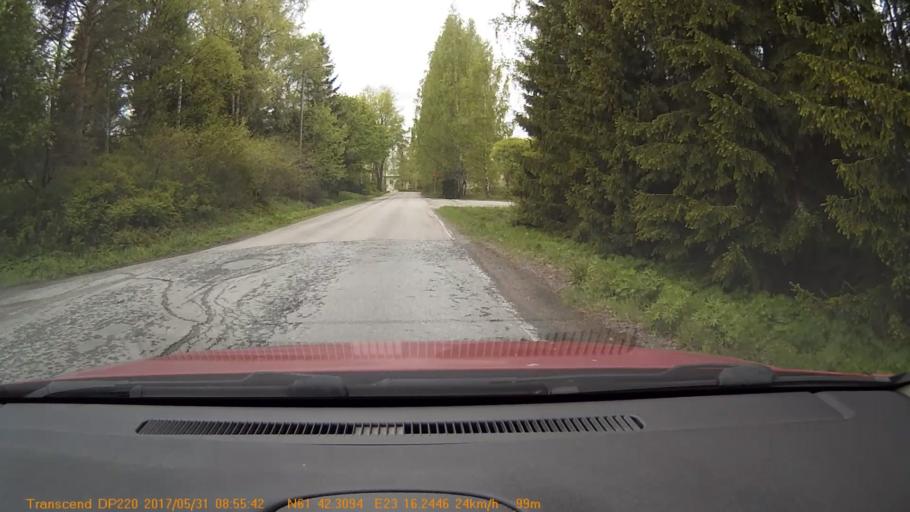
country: FI
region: Pirkanmaa
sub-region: Tampere
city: Viljakkala
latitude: 61.7051
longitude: 23.2710
